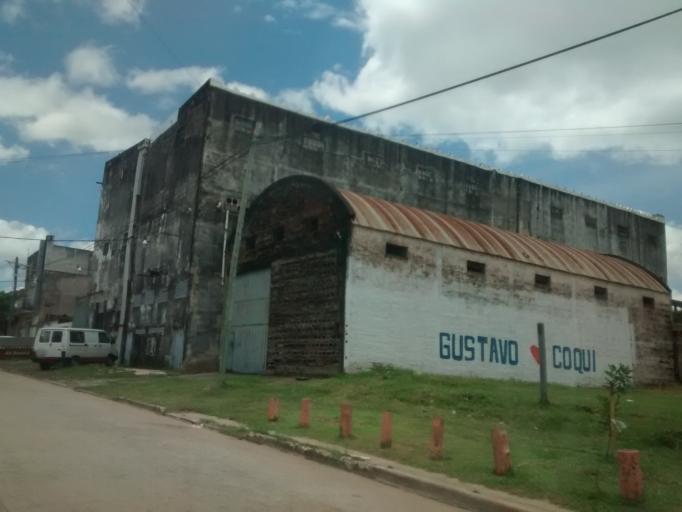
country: AR
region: Chaco
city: Fontana
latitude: -27.4347
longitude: -59.0033
